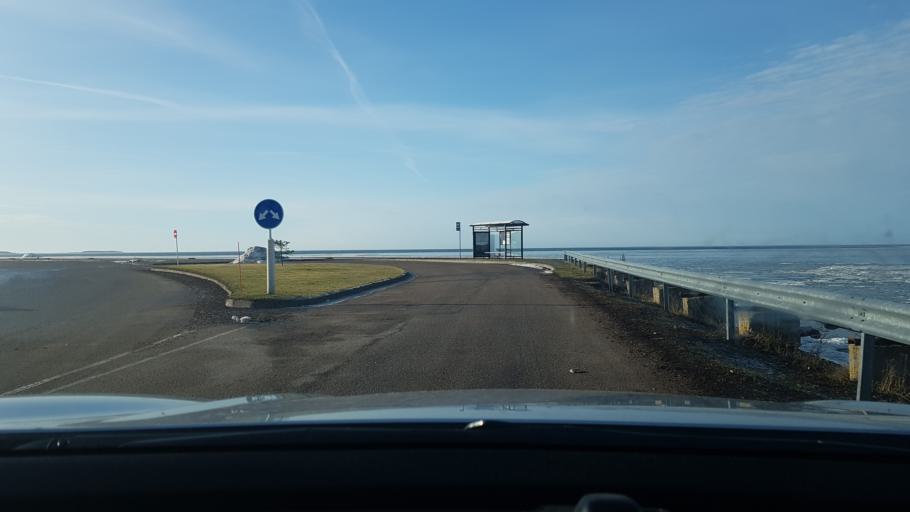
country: EE
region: Saare
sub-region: Kuressaare linn
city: Kuressaare
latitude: 58.2176
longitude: 22.5041
